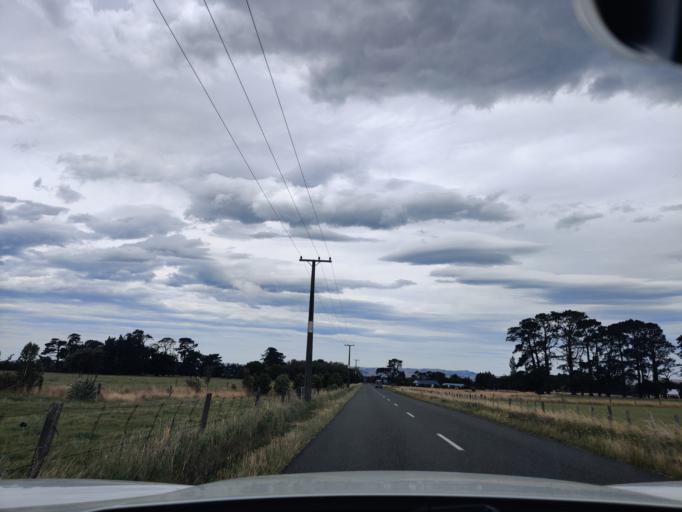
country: NZ
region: Wellington
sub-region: Masterton District
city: Masterton
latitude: -41.0216
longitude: 175.4704
